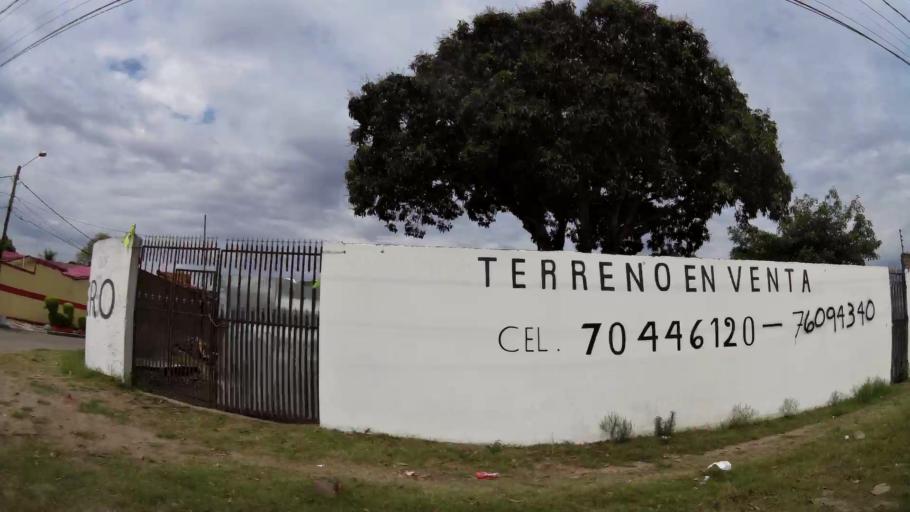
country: BO
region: Santa Cruz
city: Santa Cruz de la Sierra
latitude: -17.7723
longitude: -63.2118
